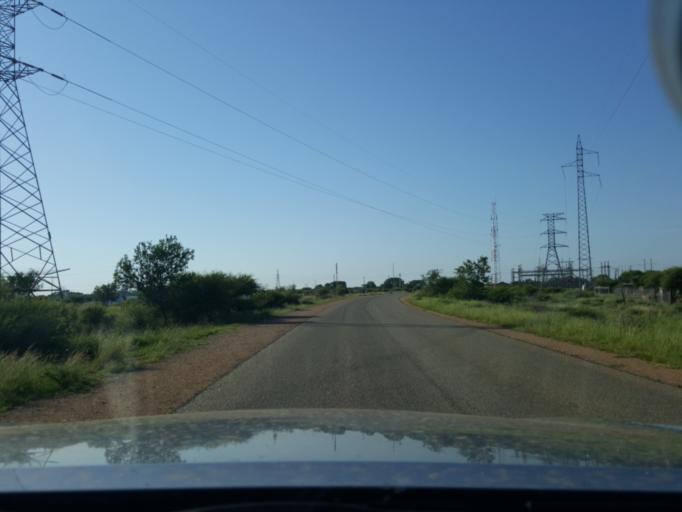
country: ZA
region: North-West
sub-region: Ngaka Modiri Molema District Municipality
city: Mahikeng
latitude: -25.8429
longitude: 25.6761
